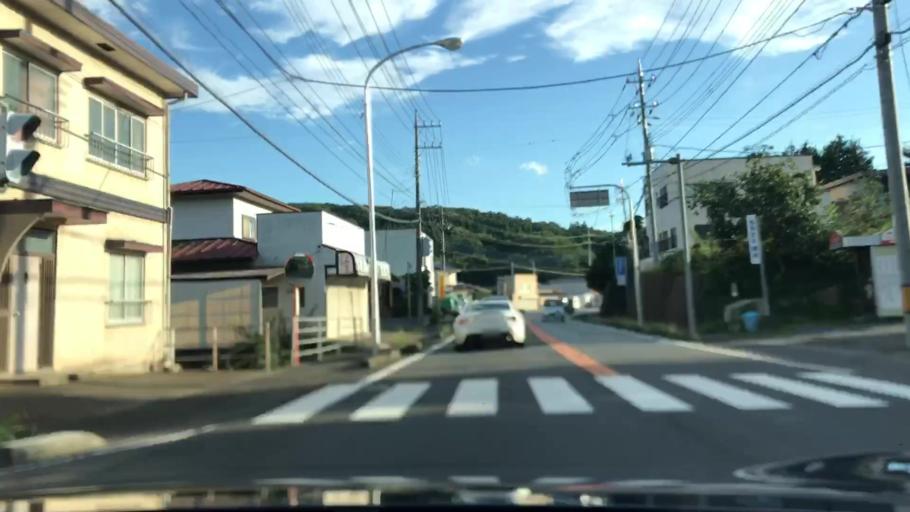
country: JP
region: Tochigi
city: Motegi
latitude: 36.5345
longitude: 140.2061
